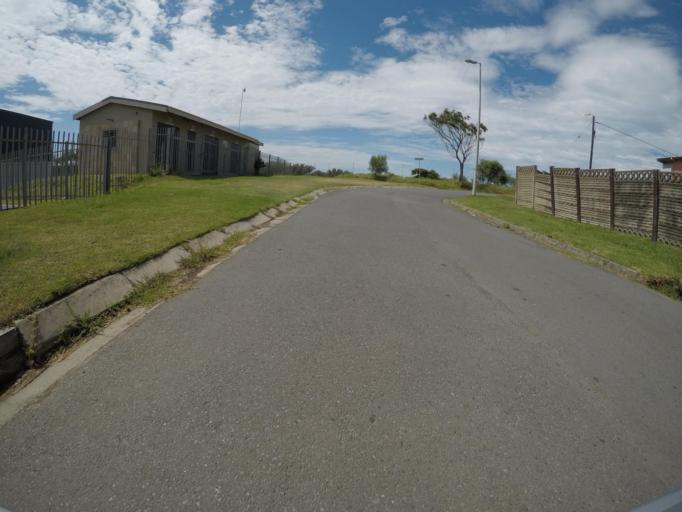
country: ZA
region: Eastern Cape
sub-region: Buffalo City Metropolitan Municipality
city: East London
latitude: -33.0386
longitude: 27.8870
